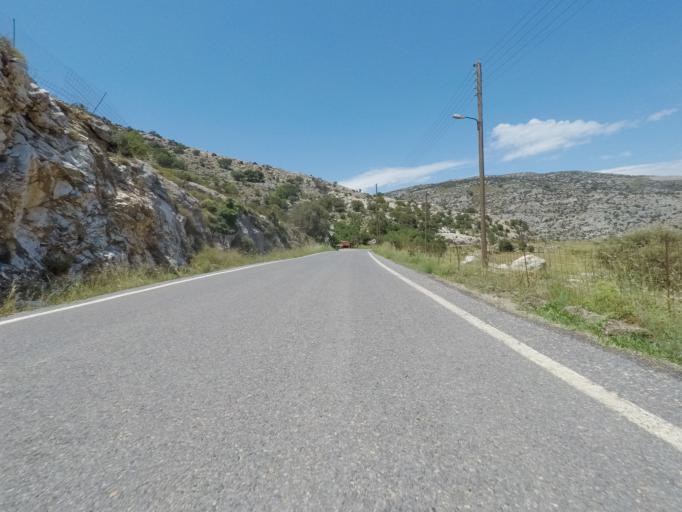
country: GR
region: Crete
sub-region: Nomos Irakleiou
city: Mokhos
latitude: 35.1872
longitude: 25.4312
